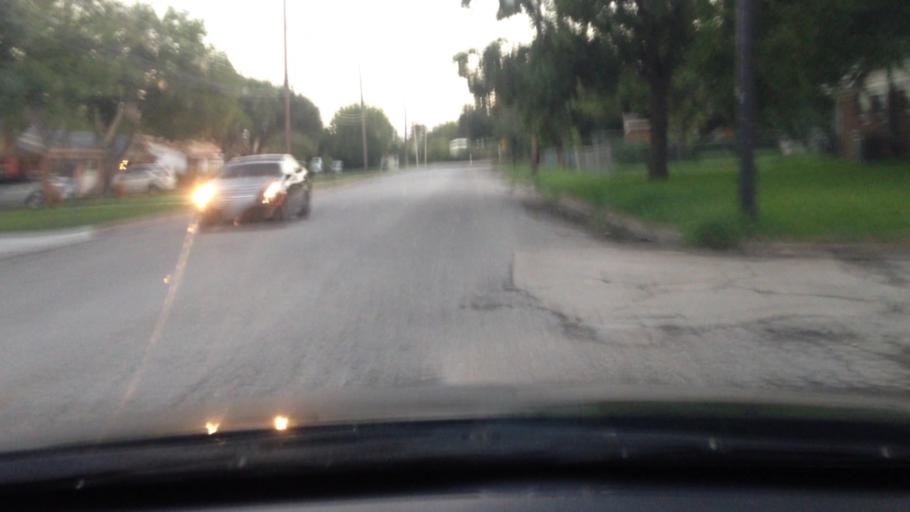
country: US
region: Texas
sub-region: Tarrant County
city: White Settlement
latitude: 32.7753
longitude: -97.4682
